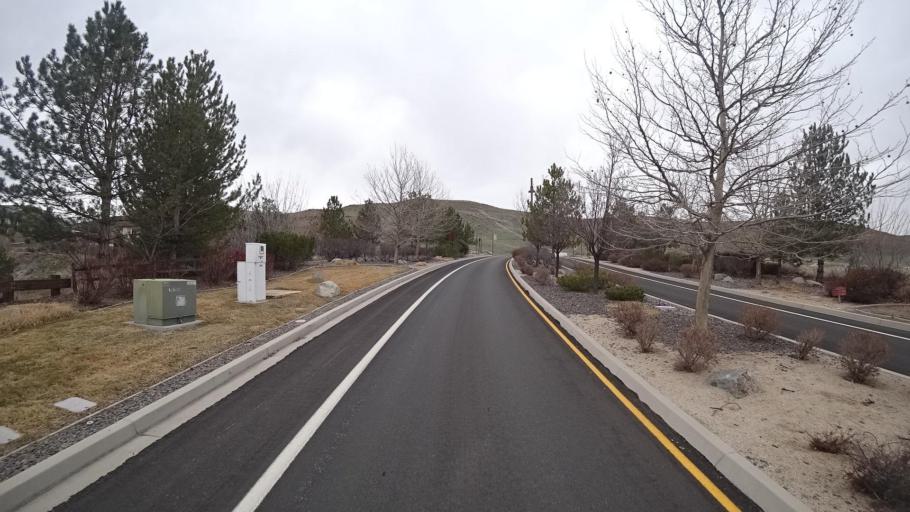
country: US
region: Nevada
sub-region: Washoe County
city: Sun Valley
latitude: 39.6029
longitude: -119.7334
